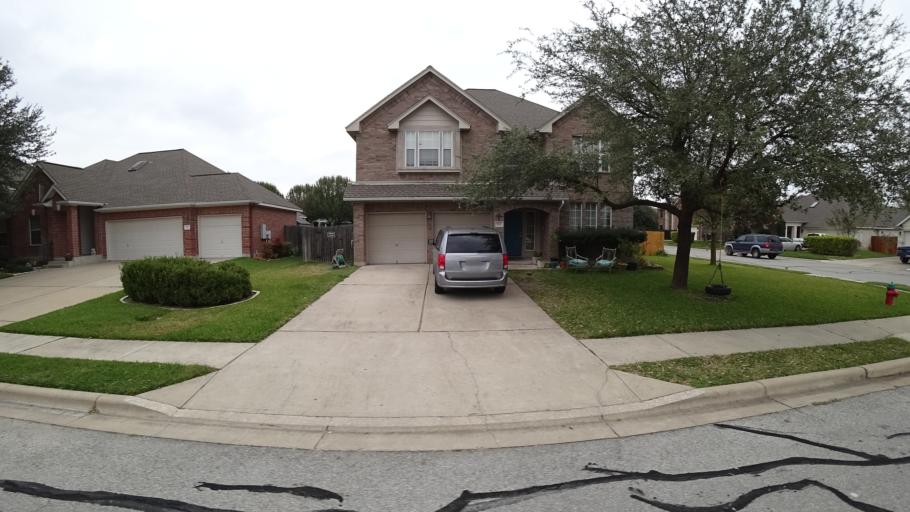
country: US
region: Texas
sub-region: Travis County
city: Pflugerville
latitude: 30.4287
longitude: -97.6166
